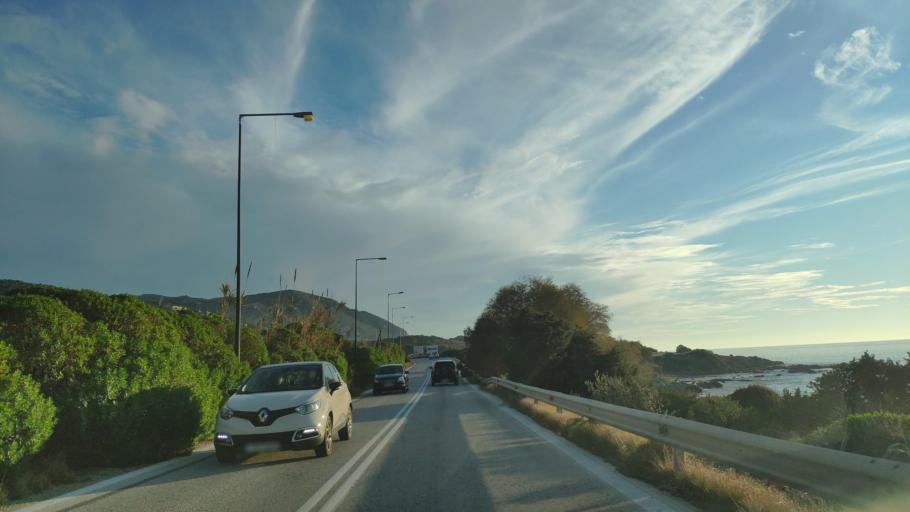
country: GR
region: Attica
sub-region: Nomarchia Anatolikis Attikis
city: Palaia Fokaia
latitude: 37.6930
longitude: 23.9383
